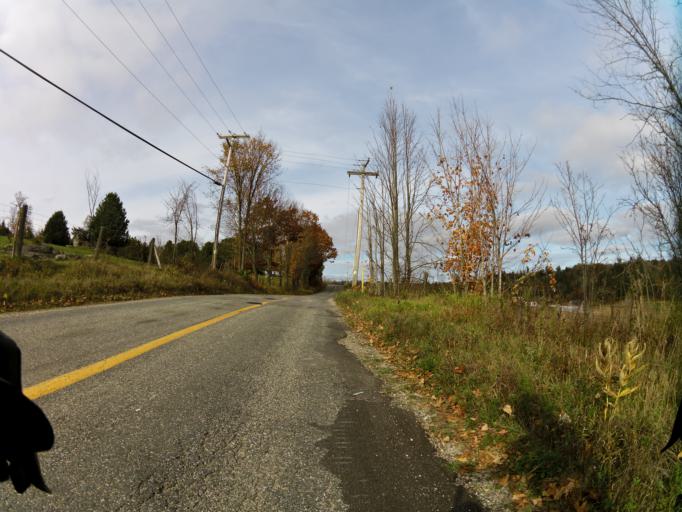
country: CA
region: Quebec
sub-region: Outaouais
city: Wakefield
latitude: 45.7337
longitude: -75.9733
